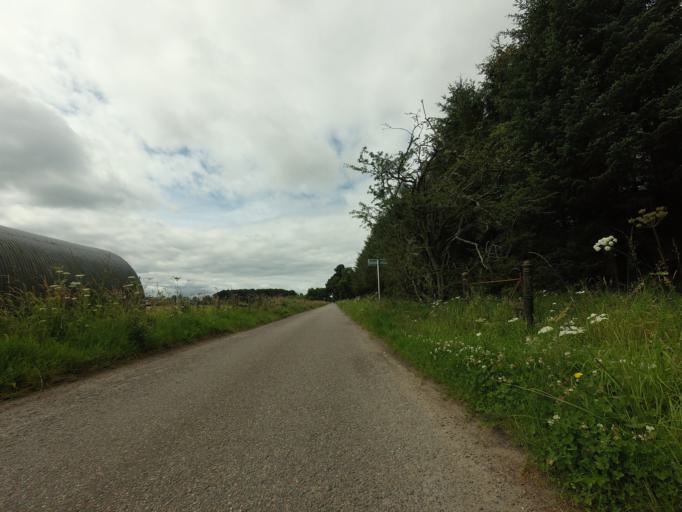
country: GB
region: Scotland
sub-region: Moray
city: Kinloss
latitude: 57.6324
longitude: -3.5773
